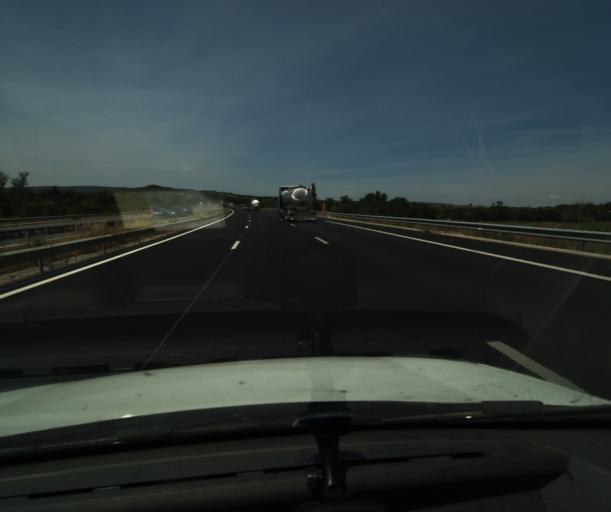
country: FR
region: Languedoc-Roussillon
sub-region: Departement de l'Aude
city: Sigean
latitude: 43.0409
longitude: 2.9500
